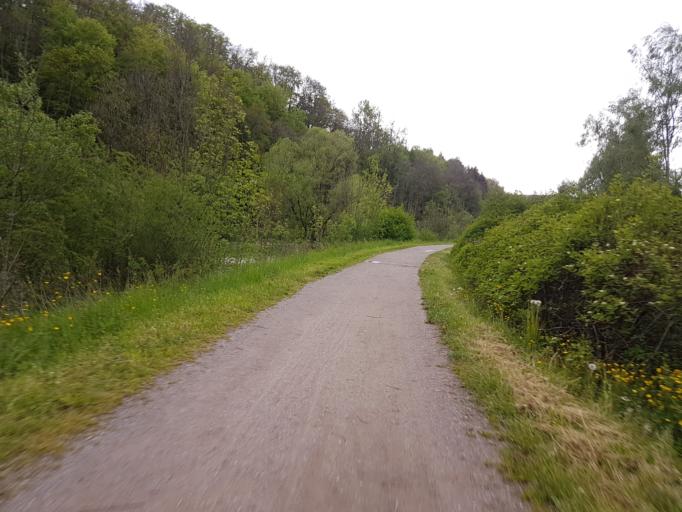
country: DE
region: Baden-Wuerttemberg
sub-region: Freiburg Region
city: Lauchringen
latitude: 47.6239
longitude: 8.3007
